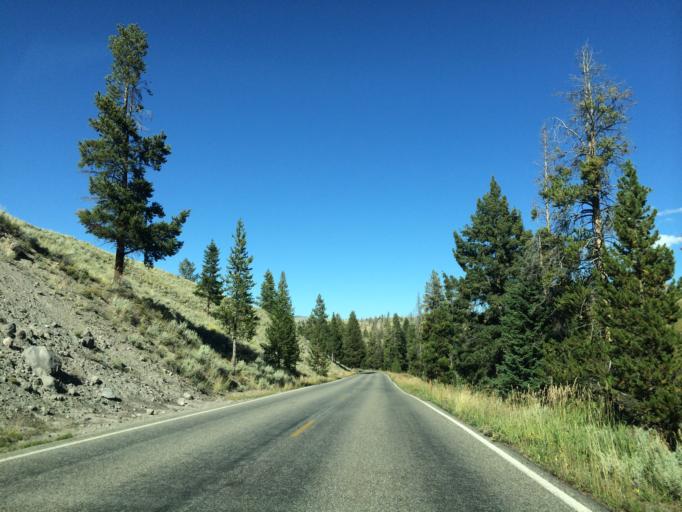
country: US
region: Montana
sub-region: Gallatin County
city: West Yellowstone
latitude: 44.8712
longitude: -110.3849
